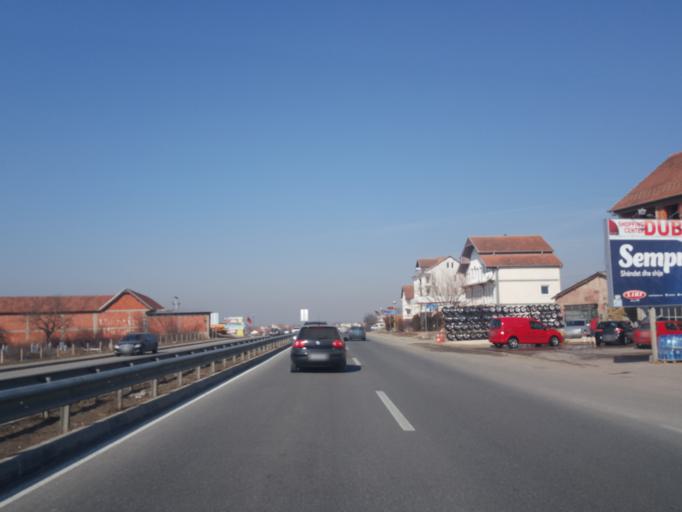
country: XK
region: Pristina
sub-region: Komuna e Obiliqit
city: Obiliq
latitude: 42.7532
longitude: 21.0386
